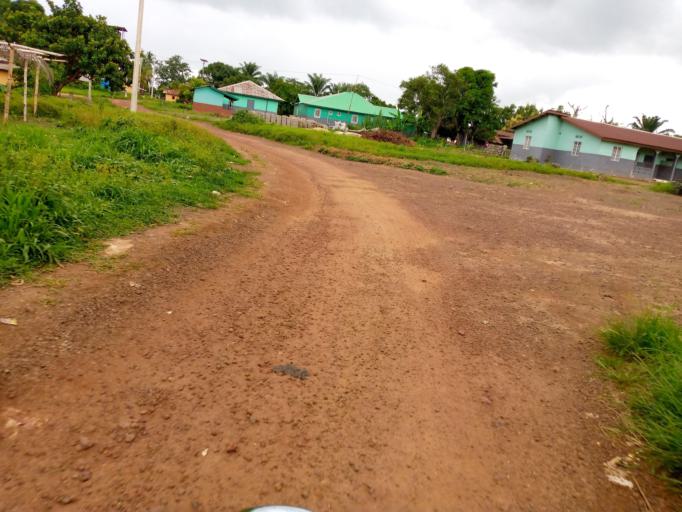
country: SL
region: Southern Province
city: Moyamba
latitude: 8.1529
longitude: -12.4352
